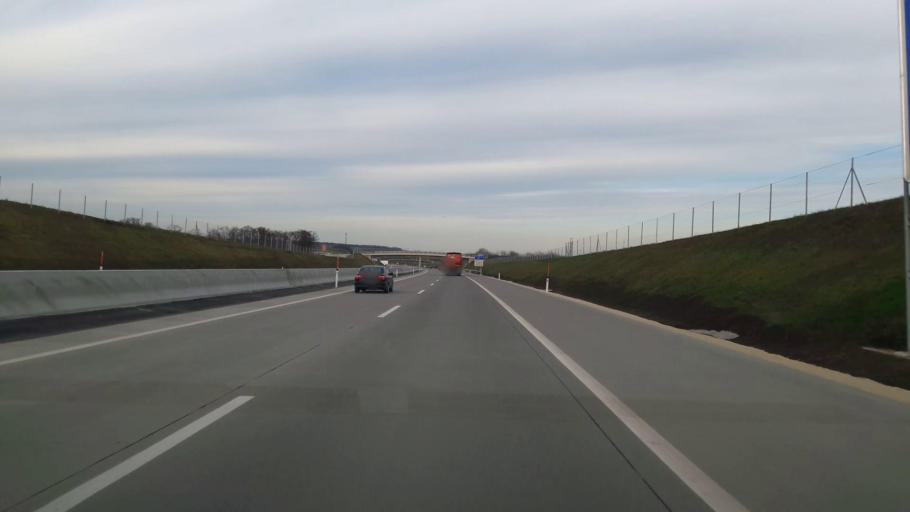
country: AT
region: Lower Austria
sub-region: Politischer Bezirk Mistelbach
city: Grosskrut
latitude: 48.6404
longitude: 16.6855
